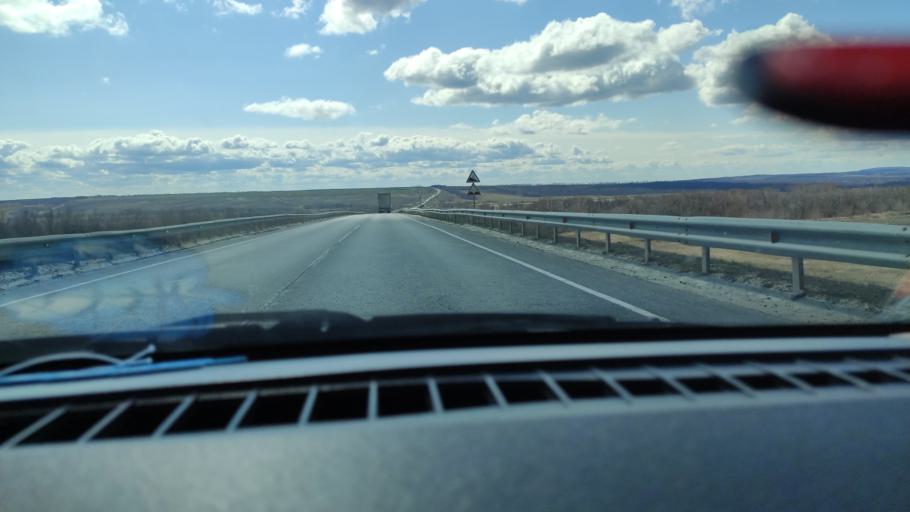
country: RU
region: Saratov
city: Dukhovnitskoye
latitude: 52.7493
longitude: 48.2493
